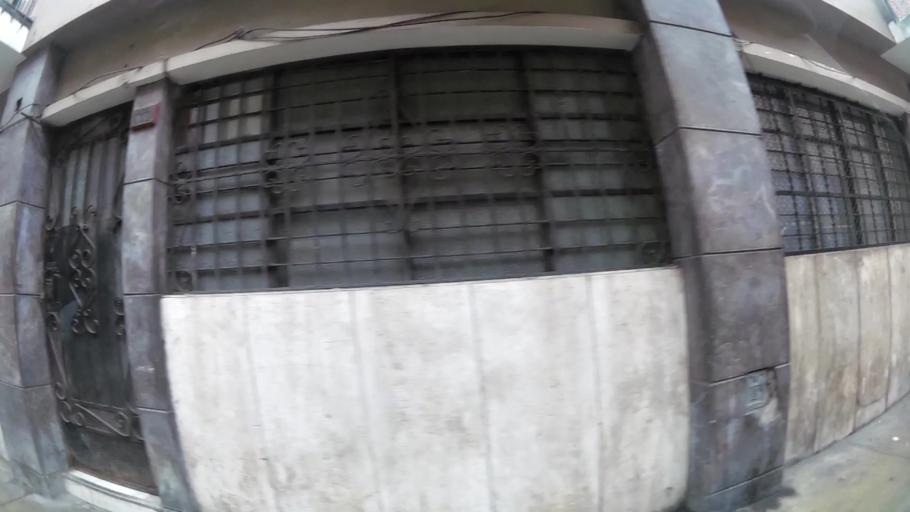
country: PE
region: Lima
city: Lima
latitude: -12.0624
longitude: -77.0396
